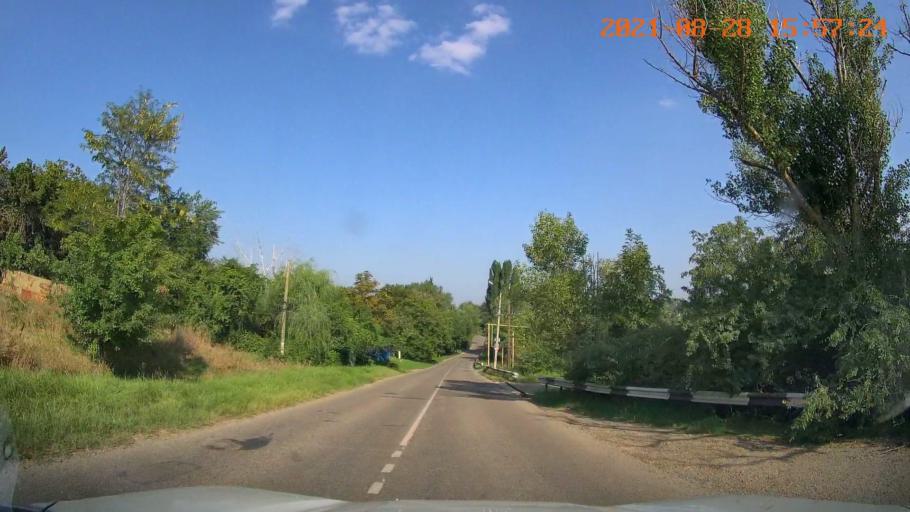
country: RU
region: Stavropol'skiy
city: Tatarka
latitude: 44.9600
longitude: 41.9407
